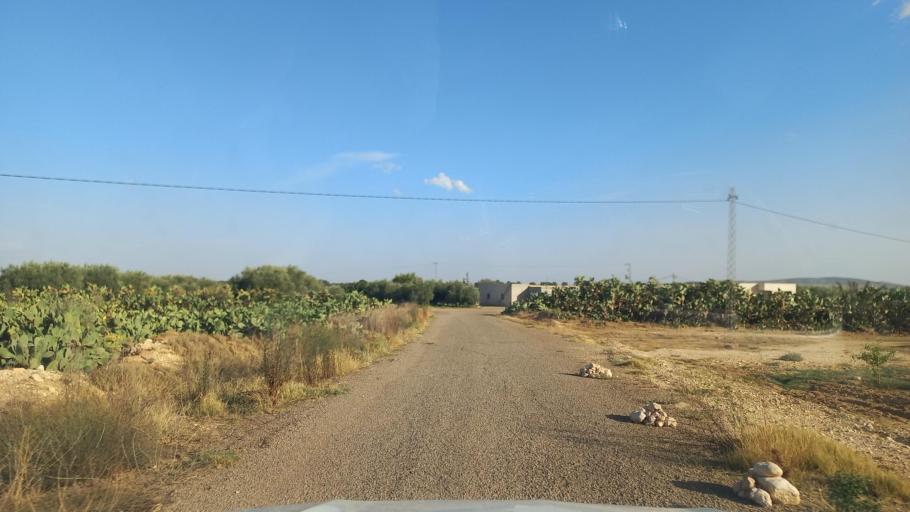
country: TN
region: Al Qasrayn
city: Kasserine
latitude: 35.2689
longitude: 9.0307
